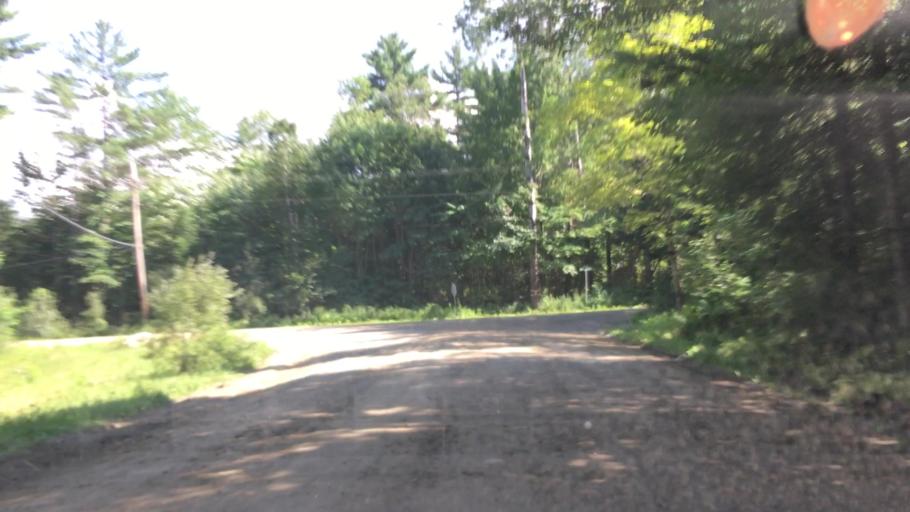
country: US
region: New Hampshire
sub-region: Grafton County
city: North Haverhill
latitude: 44.1301
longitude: -71.9635
